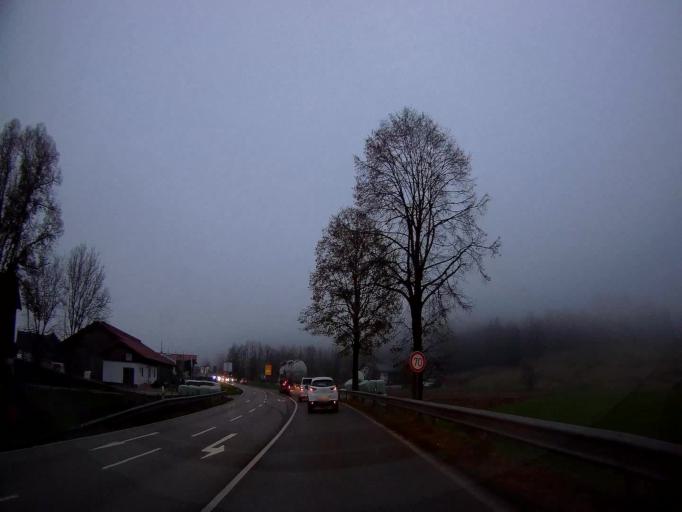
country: DE
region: Bavaria
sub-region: Upper Bavaria
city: Piding
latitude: 47.7621
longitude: 12.8997
